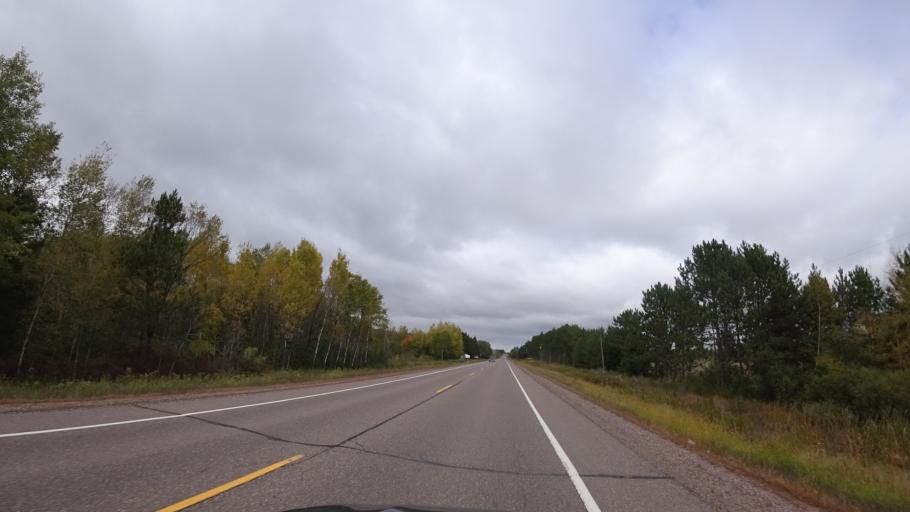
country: US
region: Wisconsin
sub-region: Rusk County
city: Ladysmith
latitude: 45.5234
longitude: -91.1115
